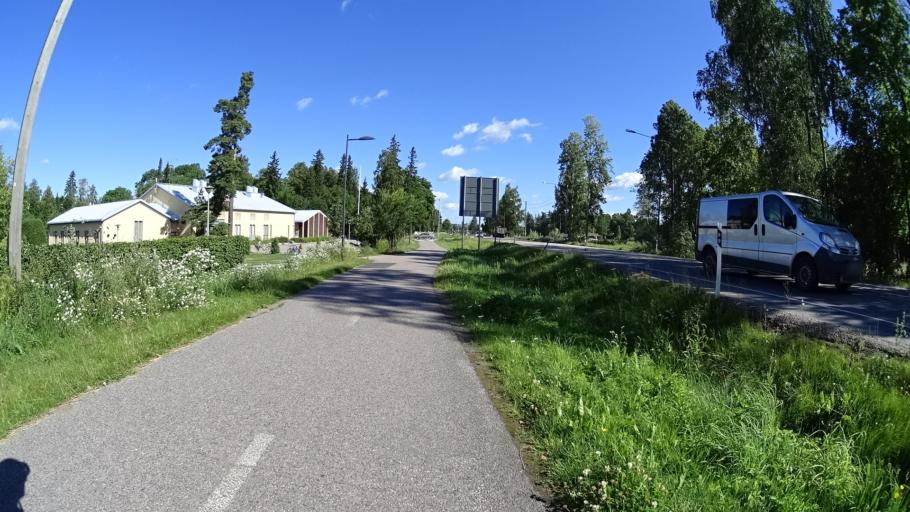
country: FI
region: Uusimaa
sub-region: Helsinki
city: Jaervenpaeae
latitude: 60.4578
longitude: 25.0840
